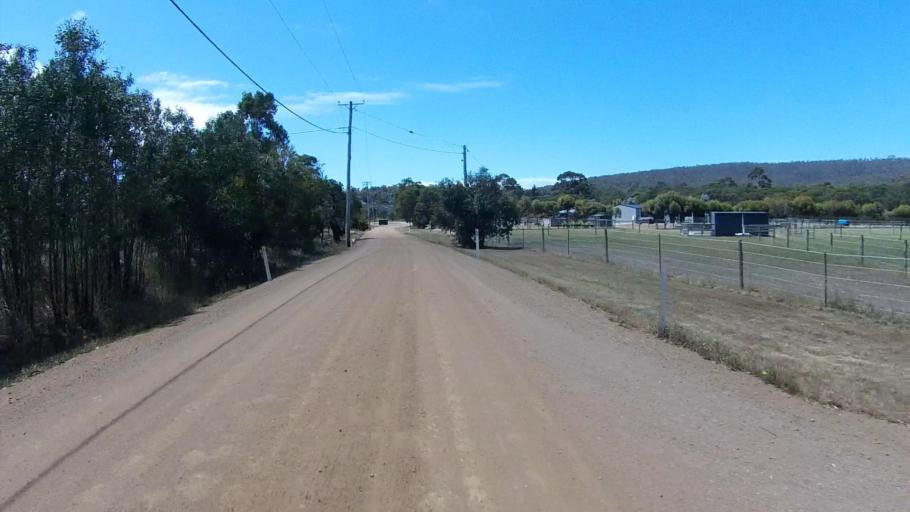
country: AU
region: Tasmania
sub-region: Clarence
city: Sandford
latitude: -42.9651
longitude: 147.4717
